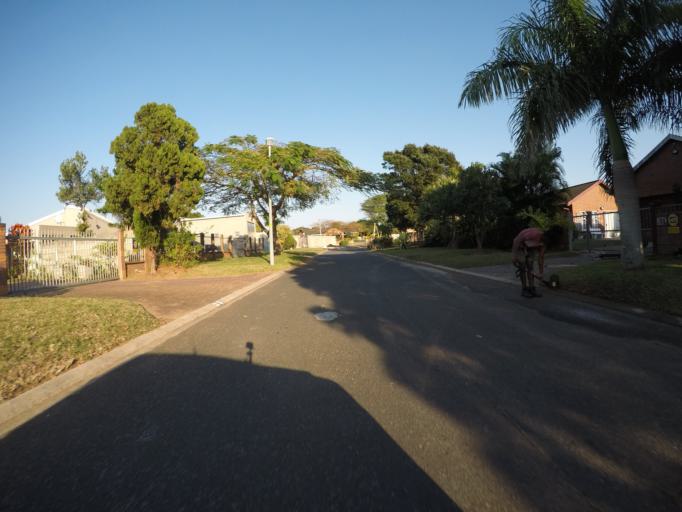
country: ZA
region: KwaZulu-Natal
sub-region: uThungulu District Municipality
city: Richards Bay
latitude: -28.7802
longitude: 32.1131
